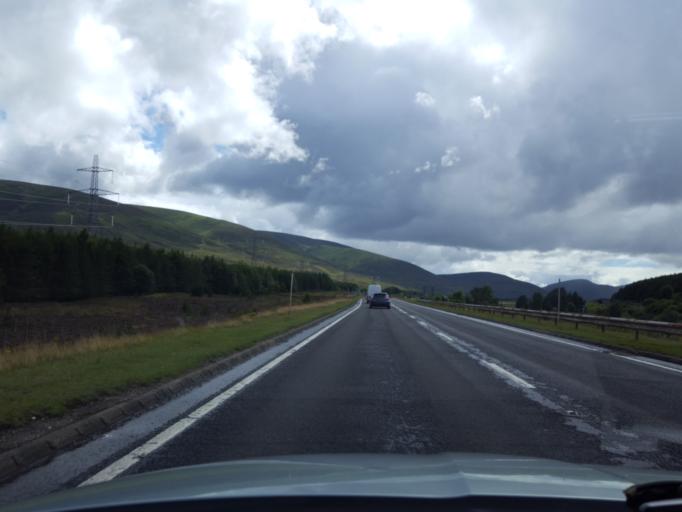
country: GB
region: Scotland
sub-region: Highland
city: Kingussie
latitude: 56.9207
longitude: -4.2361
